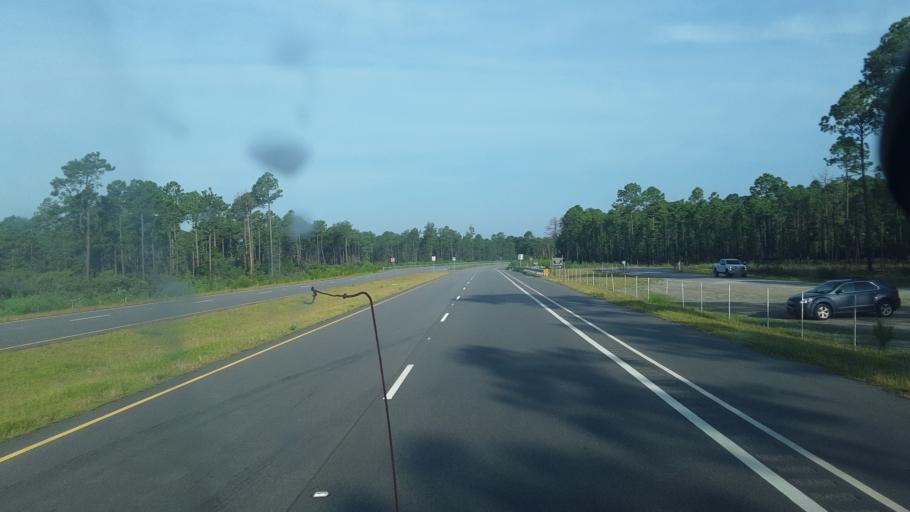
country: US
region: South Carolina
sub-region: Horry County
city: Forestbrook
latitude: 33.8054
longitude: -78.8908
